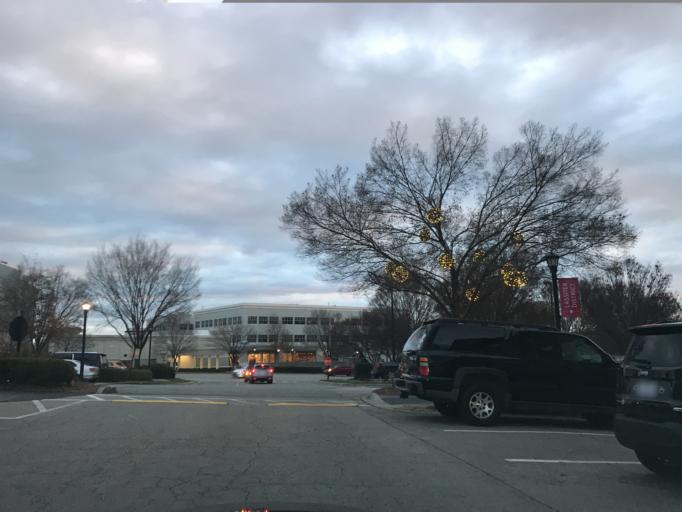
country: US
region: North Carolina
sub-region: Wake County
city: West Raleigh
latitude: 35.8397
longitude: -78.6443
